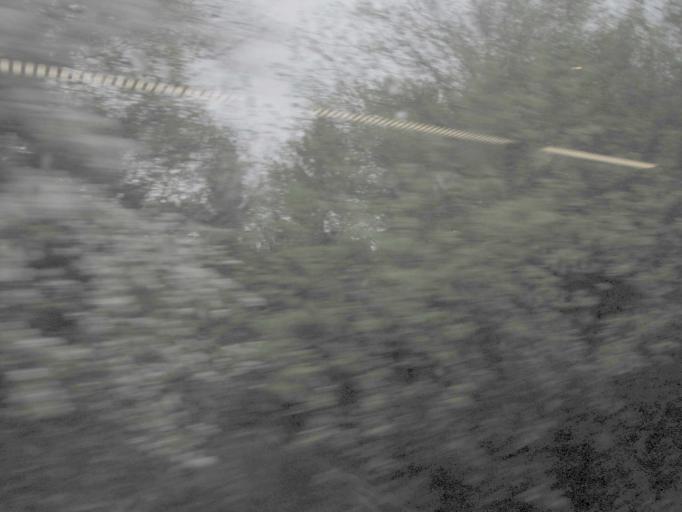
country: GB
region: England
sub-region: Wokingham
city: Wokingham
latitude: 51.4190
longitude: -0.8513
